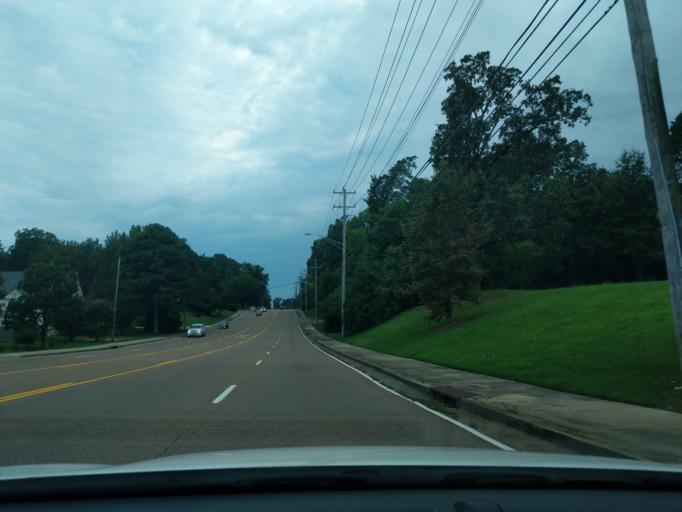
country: US
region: Tennessee
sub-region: Shelby County
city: Germantown
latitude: 35.0831
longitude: -89.8116
